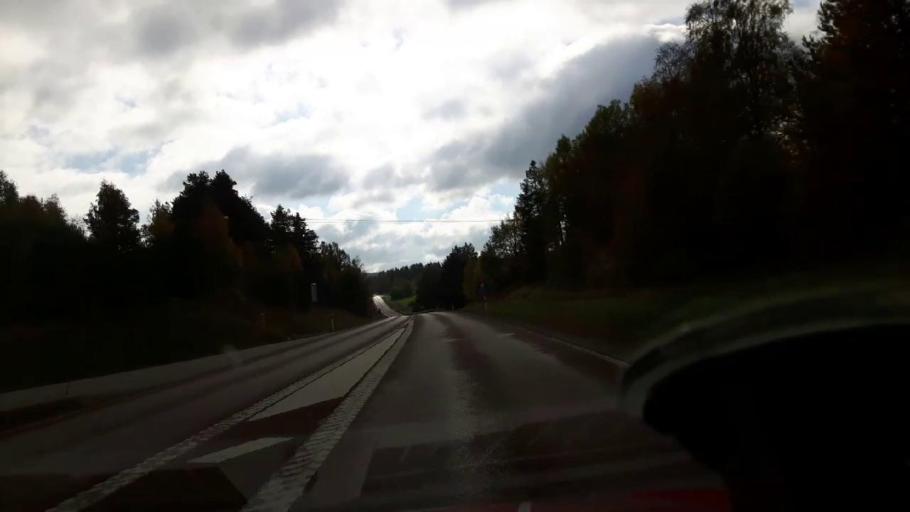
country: SE
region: Gaevleborg
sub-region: Ljusdals Kommun
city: Jaervsoe
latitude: 61.6711
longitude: 16.1459
